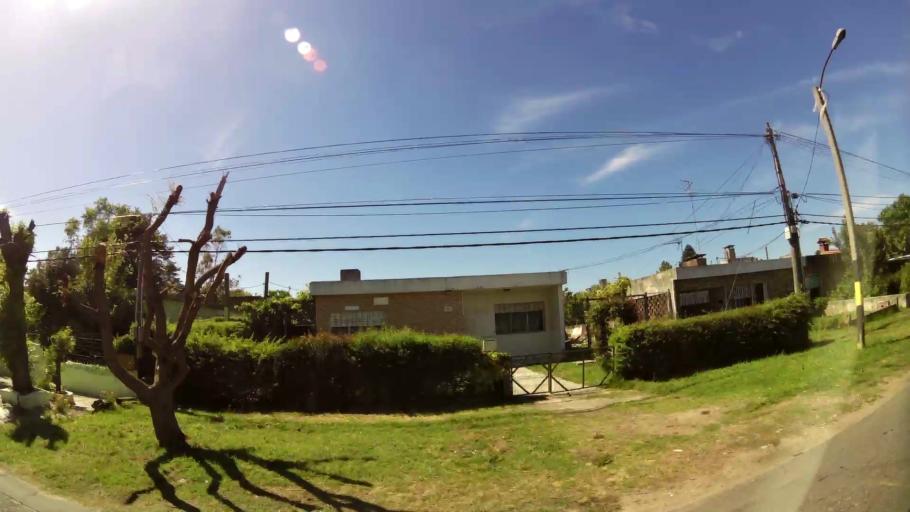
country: UY
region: Canelones
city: Paso de Carrasco
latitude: -34.8627
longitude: -56.1142
